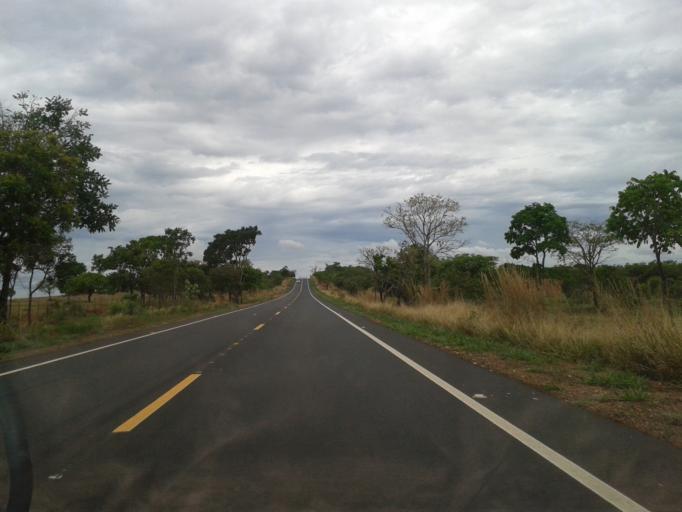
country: BR
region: Goias
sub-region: Caldas Novas
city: Caldas Novas
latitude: -17.8700
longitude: -48.6444
